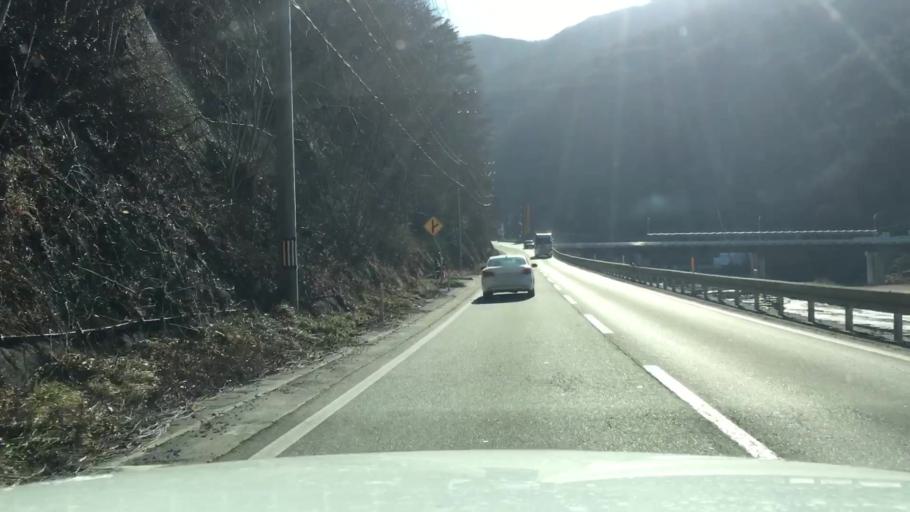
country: JP
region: Iwate
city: Miyako
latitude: 39.6177
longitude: 141.7952
